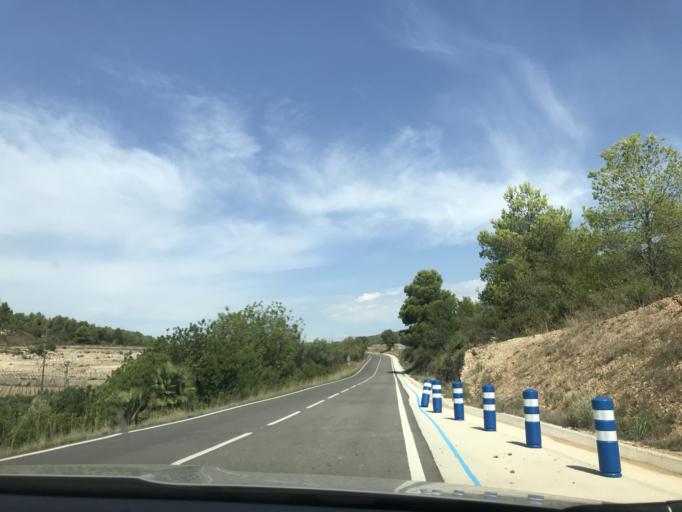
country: ES
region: Catalonia
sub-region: Provincia de Tarragona
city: Salomo
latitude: 41.2185
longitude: 1.3800
